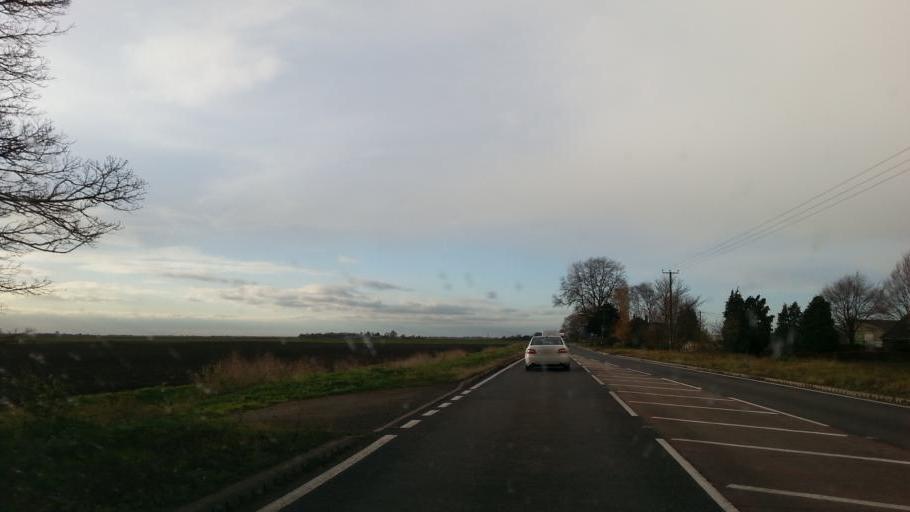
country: GB
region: England
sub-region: Peterborough
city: Thorney
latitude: 52.6145
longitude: -0.0002
